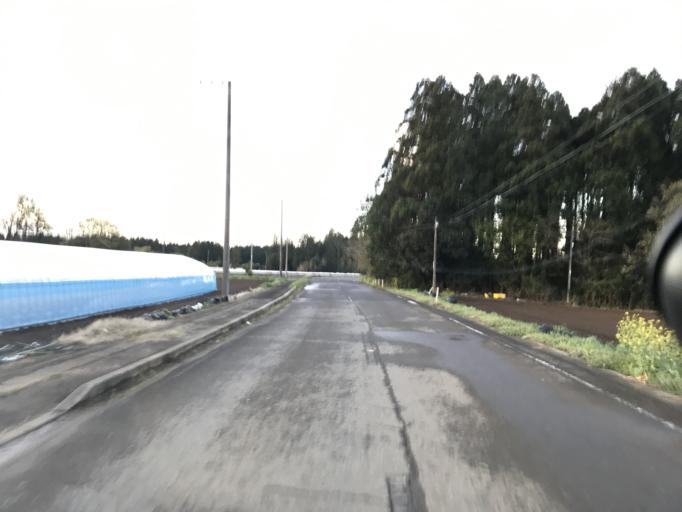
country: JP
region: Chiba
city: Sawara
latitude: 35.8259
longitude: 140.4961
